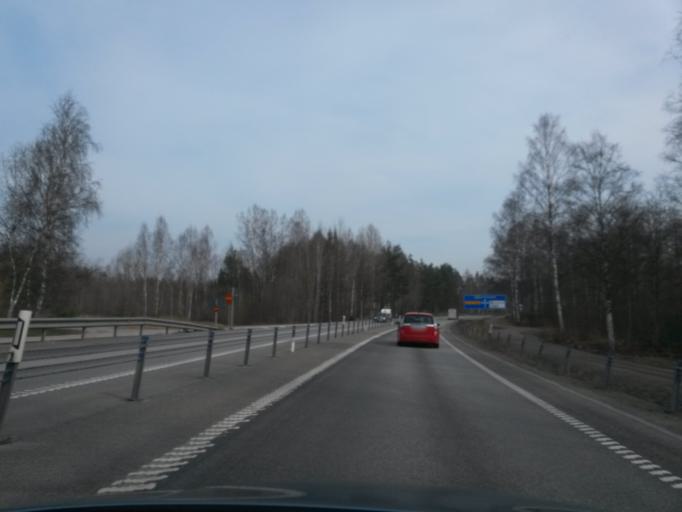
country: SE
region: OErebro
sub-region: Laxa Kommun
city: Laxa
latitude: 58.9707
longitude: 14.5402
